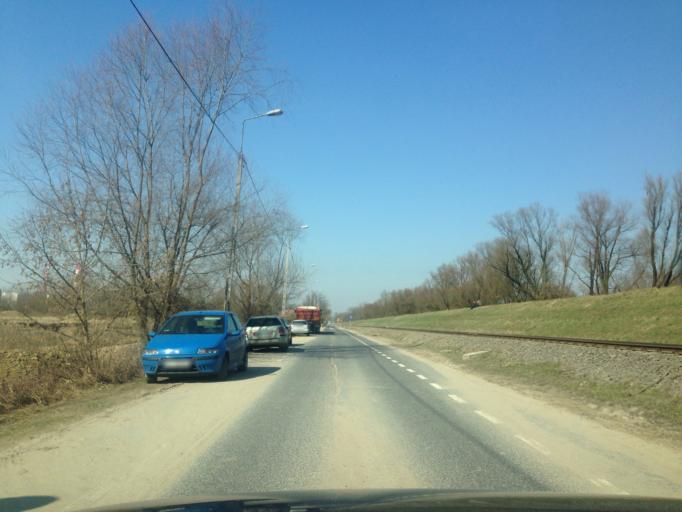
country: PL
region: Masovian Voivodeship
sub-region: Warszawa
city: Wilanow
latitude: 52.1738
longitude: 21.1193
